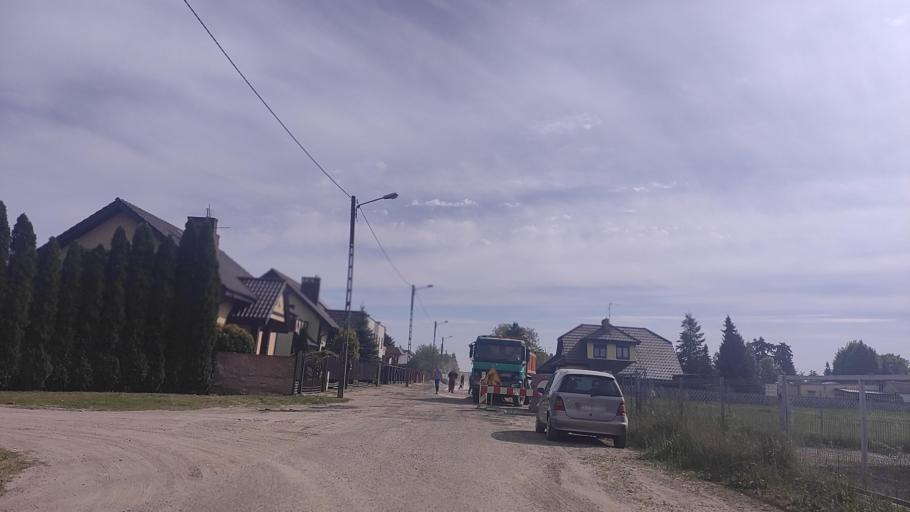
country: PL
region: Greater Poland Voivodeship
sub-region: Powiat poznanski
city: Swarzedz
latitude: 52.4116
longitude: 17.0968
